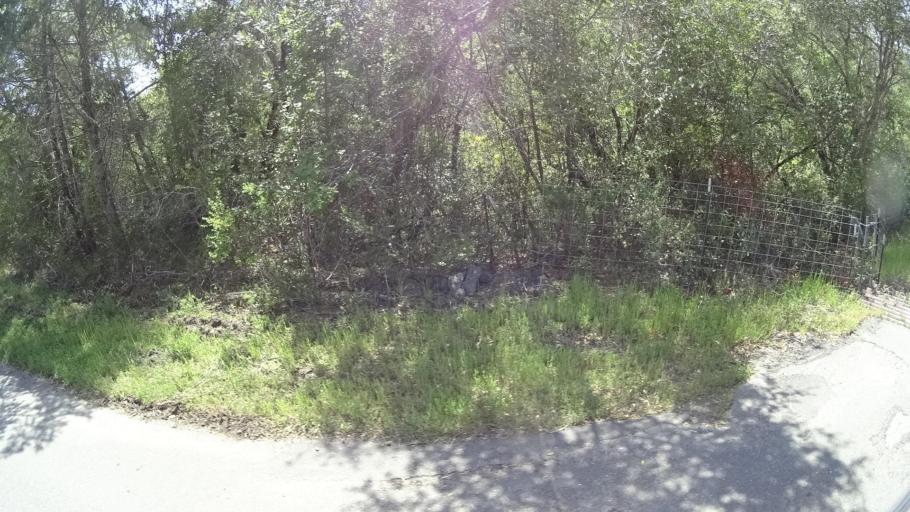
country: US
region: California
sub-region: Humboldt County
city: Redway
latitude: 40.2370
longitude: -123.6343
